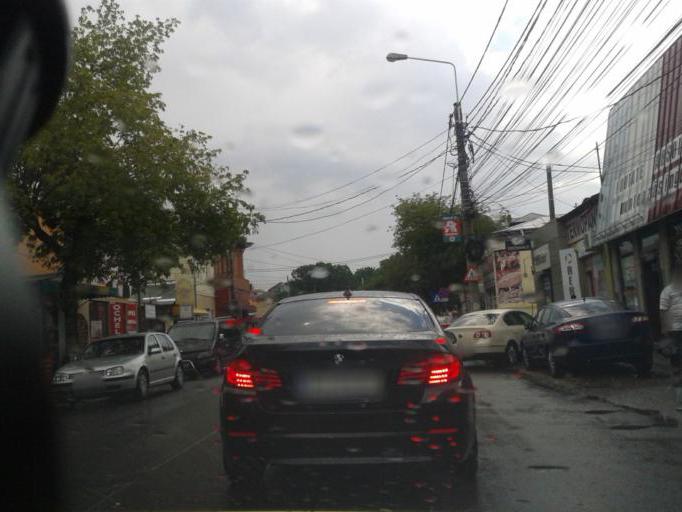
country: RO
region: Prahova
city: Ploiesti
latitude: 44.9452
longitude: 26.0231
